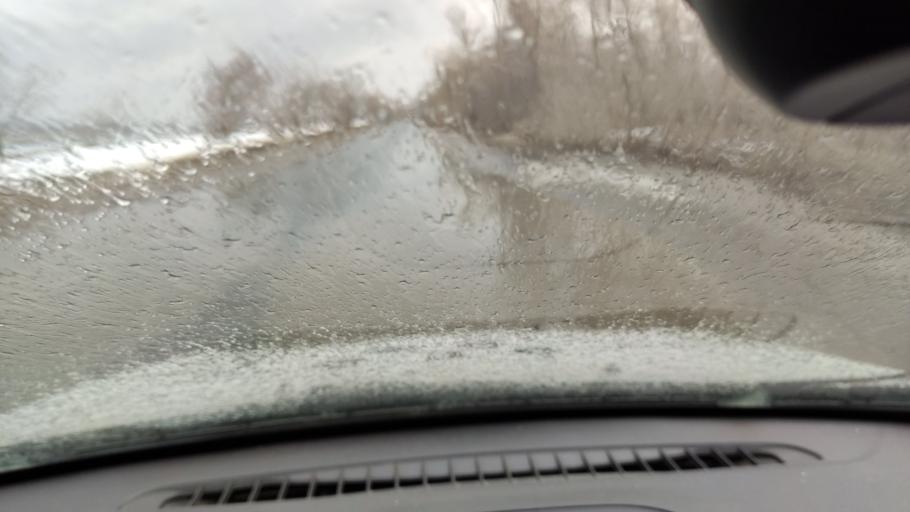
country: RU
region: Samara
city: Zhigulevsk
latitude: 53.4584
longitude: 49.5321
